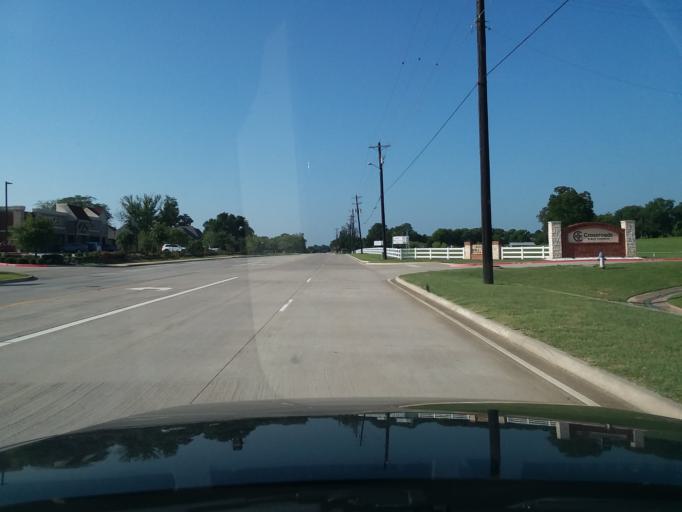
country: US
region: Texas
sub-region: Denton County
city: Double Oak
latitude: 33.0706
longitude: -97.0881
